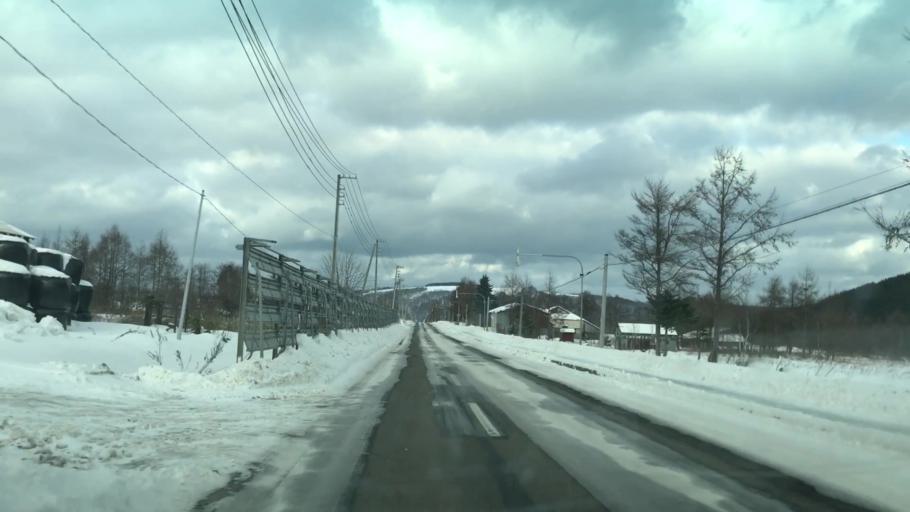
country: JP
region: Hokkaido
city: Yoichi
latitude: 43.3067
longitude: 140.5555
